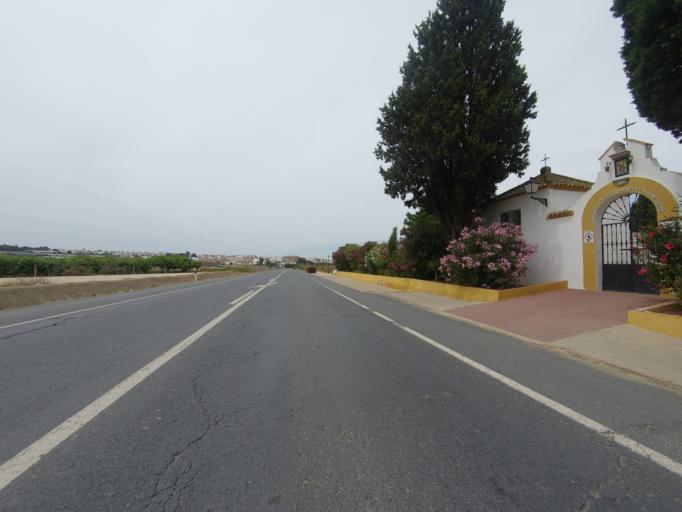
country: ES
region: Andalusia
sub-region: Provincia de Huelva
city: Palos de la Frontera
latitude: 37.2358
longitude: -6.8869
